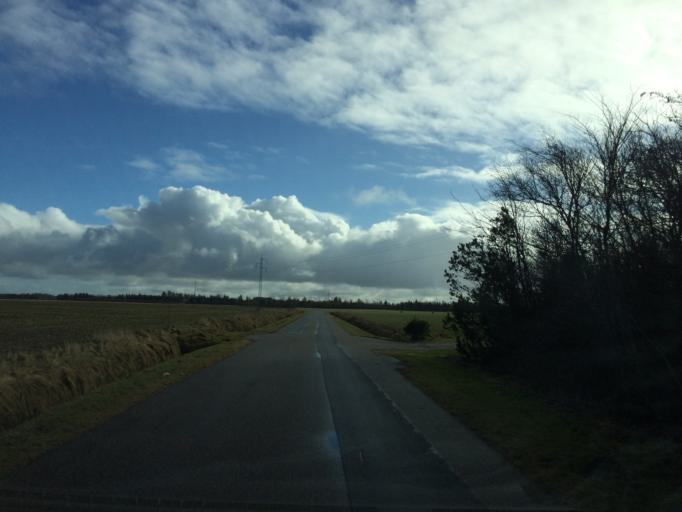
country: DK
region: Central Jutland
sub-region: Holstebro Kommune
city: Ulfborg
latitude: 56.2814
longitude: 8.3347
